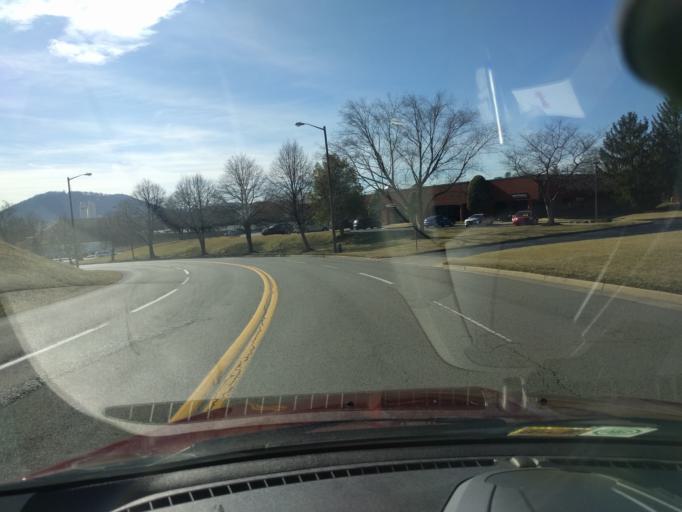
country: US
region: Virginia
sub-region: City of Roanoke
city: Roanoke
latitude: 37.2839
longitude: -79.9297
